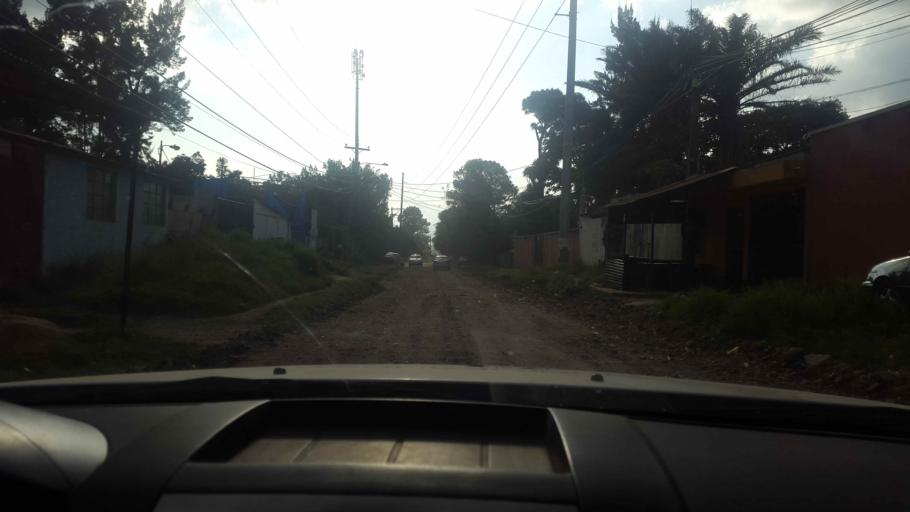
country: GT
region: Guatemala
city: Petapa
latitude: 14.5155
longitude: -90.5431
